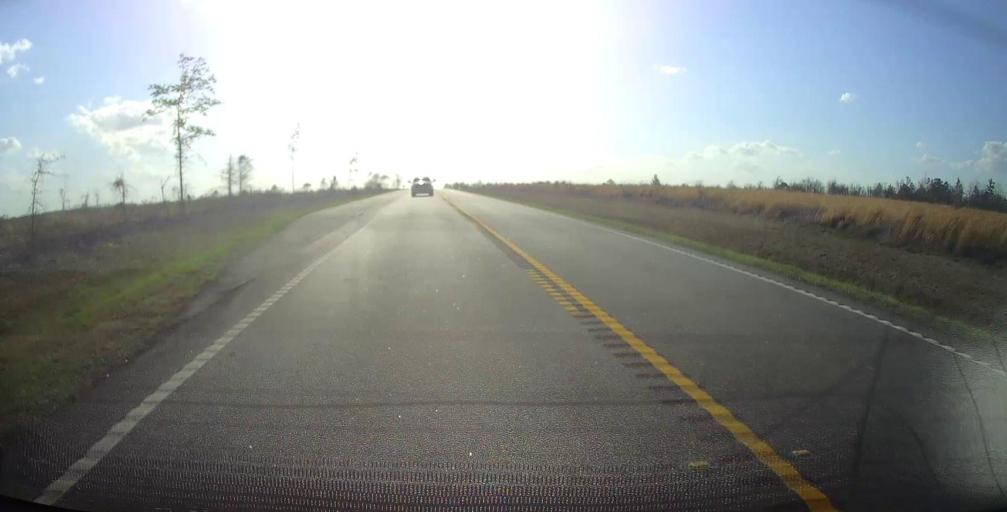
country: US
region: Georgia
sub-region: Montgomery County
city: Mount Vernon
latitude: 32.1840
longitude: -82.5403
